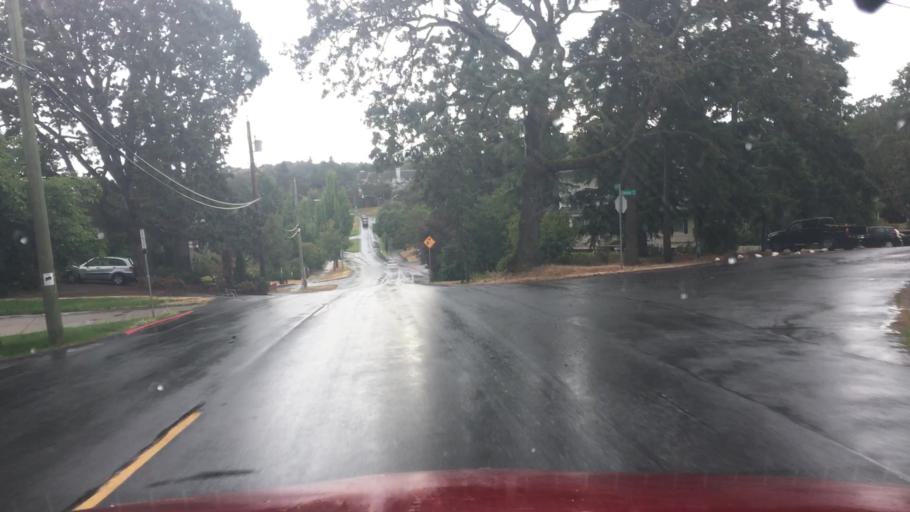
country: CA
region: British Columbia
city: Victoria
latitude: 48.4532
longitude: -123.3506
